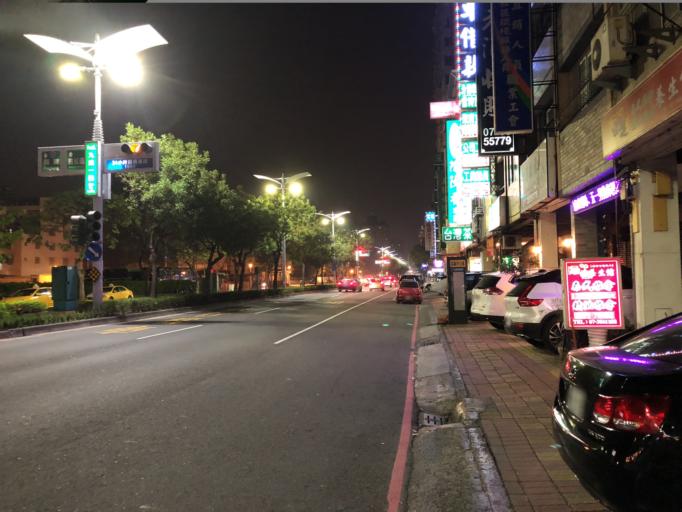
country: TW
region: Kaohsiung
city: Kaohsiung
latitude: 22.6386
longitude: 120.3309
